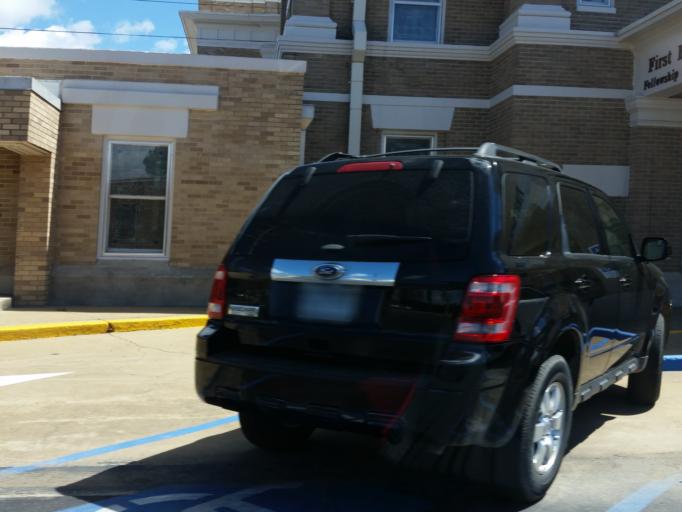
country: US
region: Arkansas
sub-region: Craighead County
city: Jonesboro
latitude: 35.8367
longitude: -90.7058
